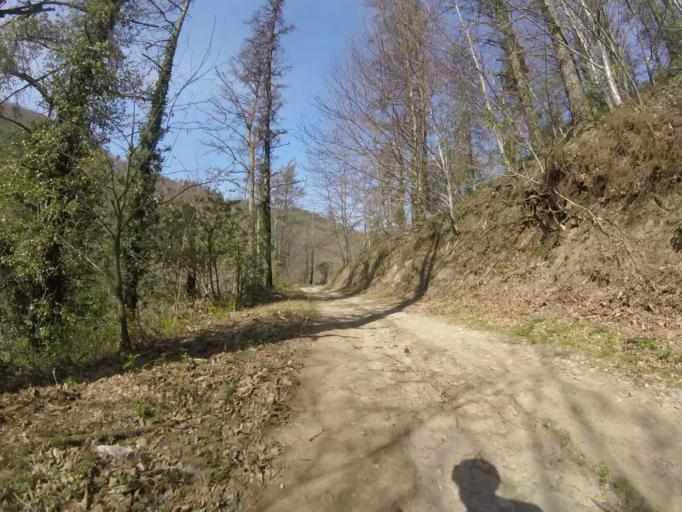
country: ES
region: Basque Country
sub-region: Provincia de Guipuzcoa
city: Irun
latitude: 43.2585
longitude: -1.8082
